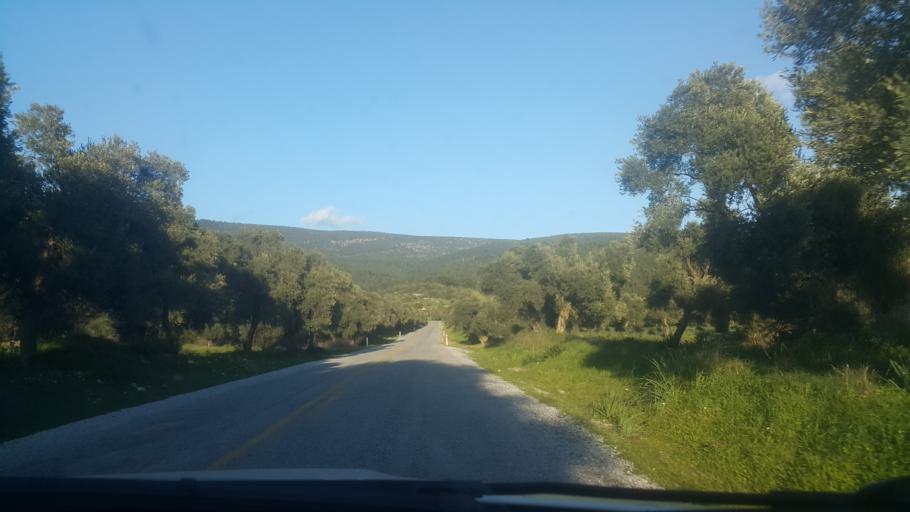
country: TR
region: Mugla
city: Kiulukioi
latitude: 37.3024
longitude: 27.6085
